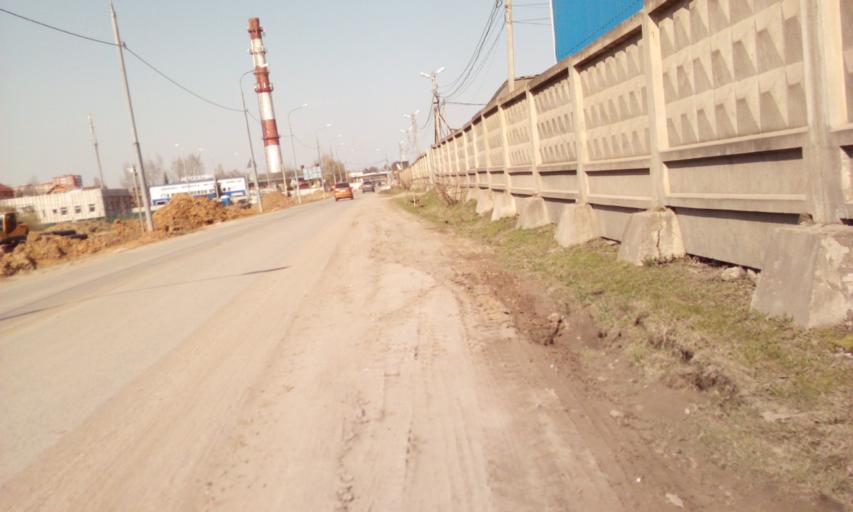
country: RU
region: Moskovskaya
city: Kommunarka
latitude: 55.5174
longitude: 37.4523
